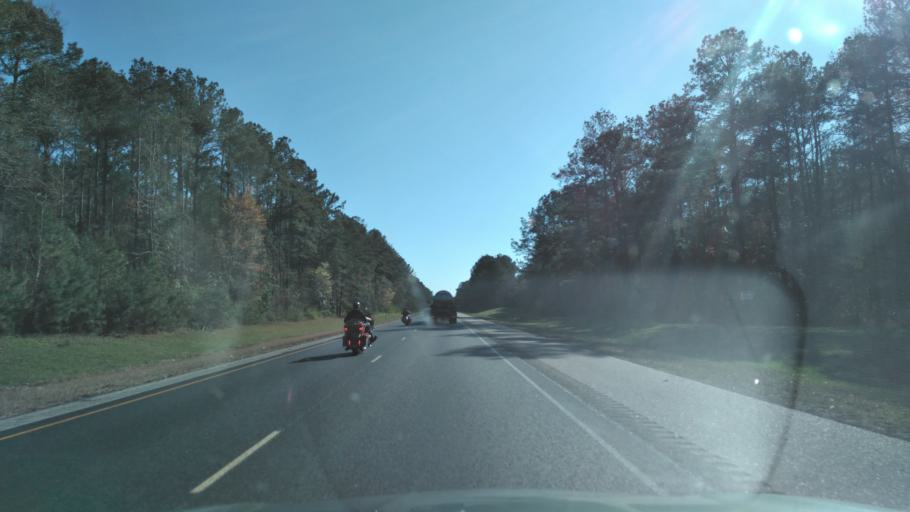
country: US
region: Alabama
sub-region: Butler County
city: Greenville
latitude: 31.7602
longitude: -86.7034
